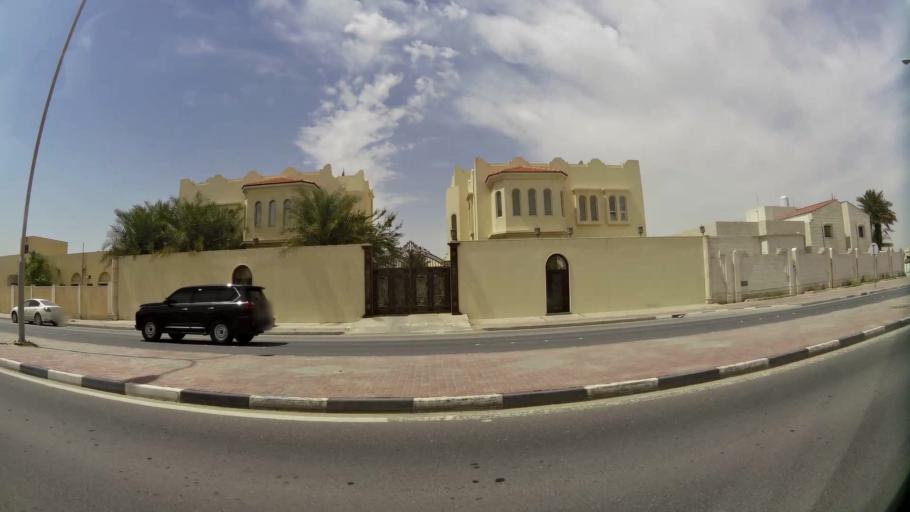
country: QA
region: Baladiyat ar Rayyan
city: Ar Rayyan
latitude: 25.2988
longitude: 51.4119
